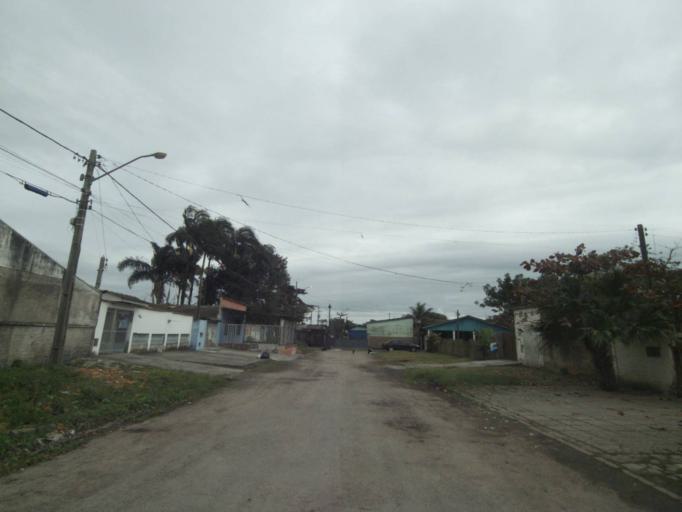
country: BR
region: Parana
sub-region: Paranagua
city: Paranagua
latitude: -25.5148
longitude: -48.5355
